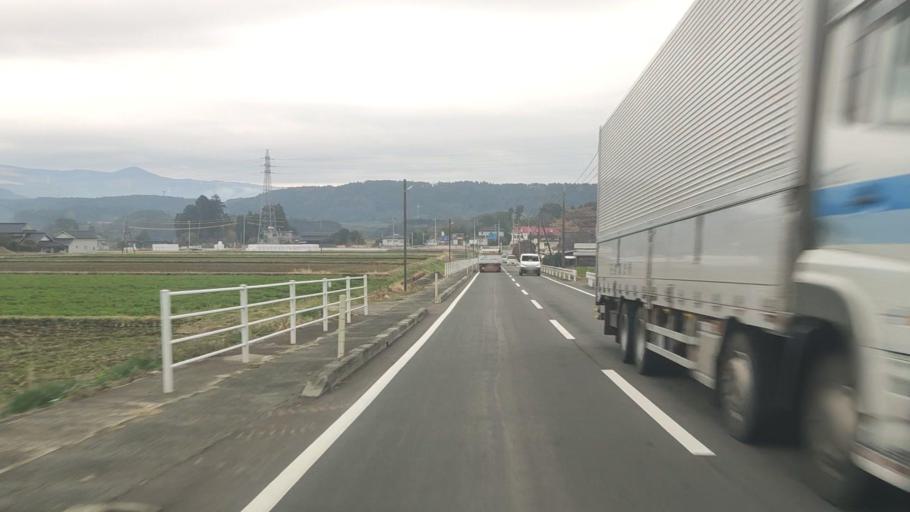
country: JP
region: Kumamoto
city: Ozu
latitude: 32.8681
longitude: 130.8903
